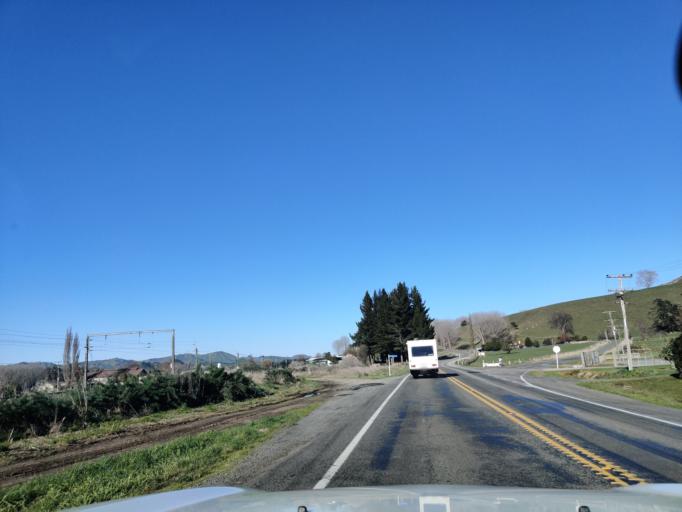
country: NZ
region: Manawatu-Wanganui
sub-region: Ruapehu District
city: Waiouru
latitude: -39.7337
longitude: 175.8436
